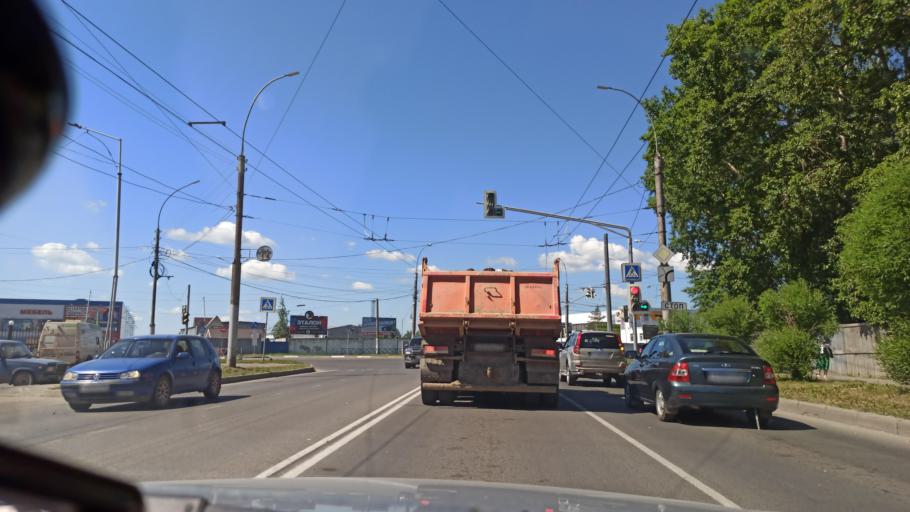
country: RU
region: Vologda
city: Vologda
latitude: 59.2009
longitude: 39.8211
